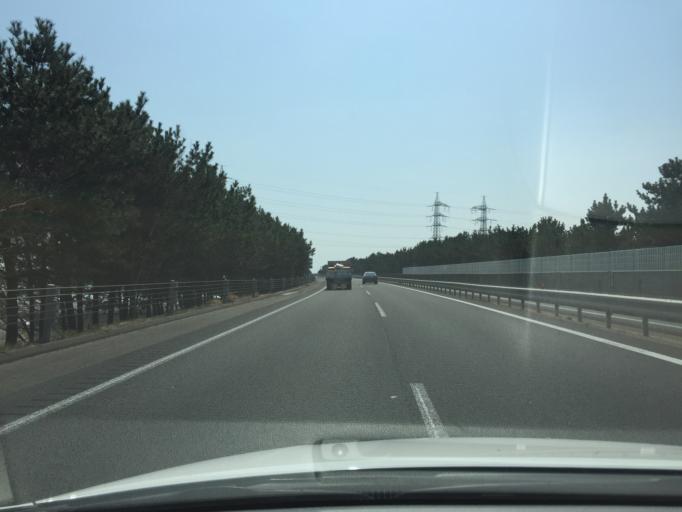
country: JP
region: Miyagi
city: Sendai-shi
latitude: 38.2377
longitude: 140.9521
